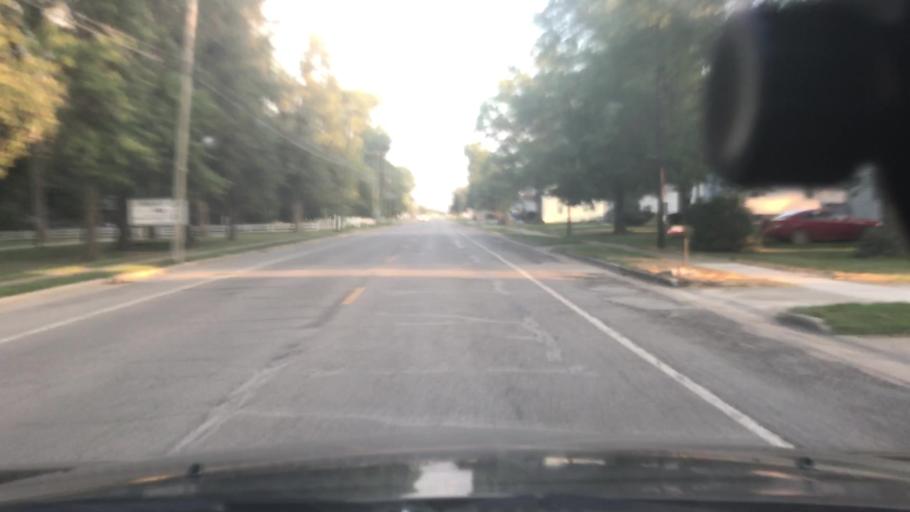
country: US
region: Illinois
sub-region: Washington County
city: Okawville
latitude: 38.4261
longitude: -89.5506
